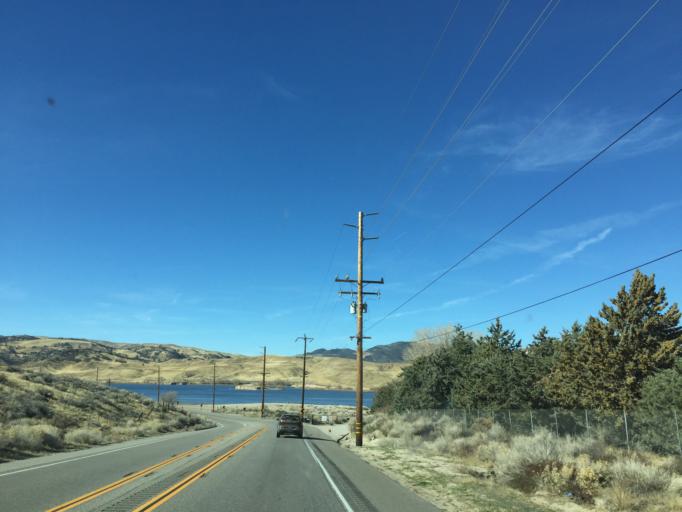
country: US
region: California
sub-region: Kern County
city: Lebec
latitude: 34.7667
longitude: -118.7363
